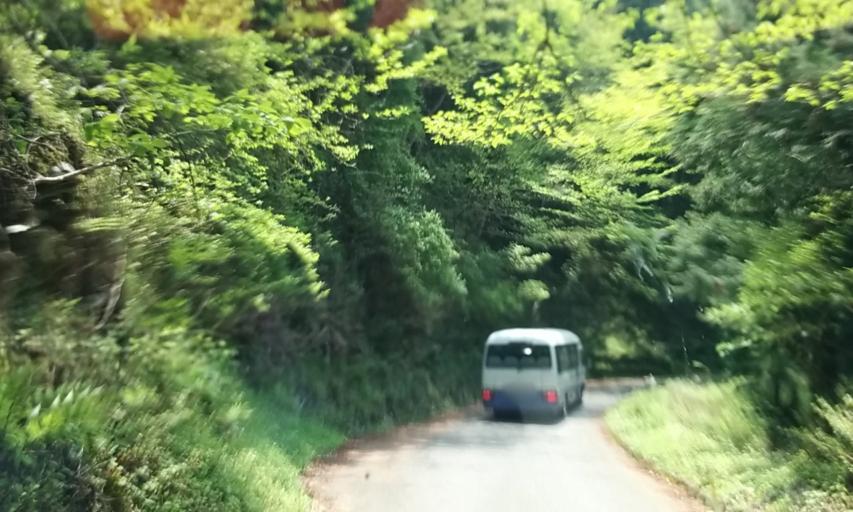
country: JP
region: Ehime
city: Niihama
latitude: 33.8787
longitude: 133.3103
